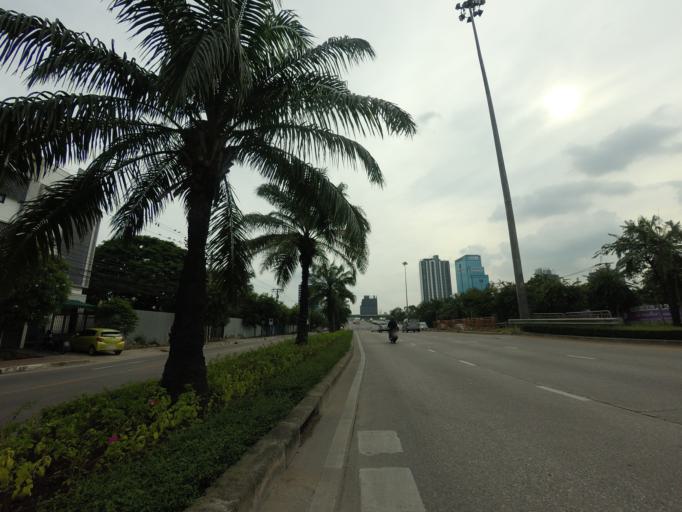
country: TH
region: Bangkok
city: Watthana
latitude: 13.7476
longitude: 100.5921
